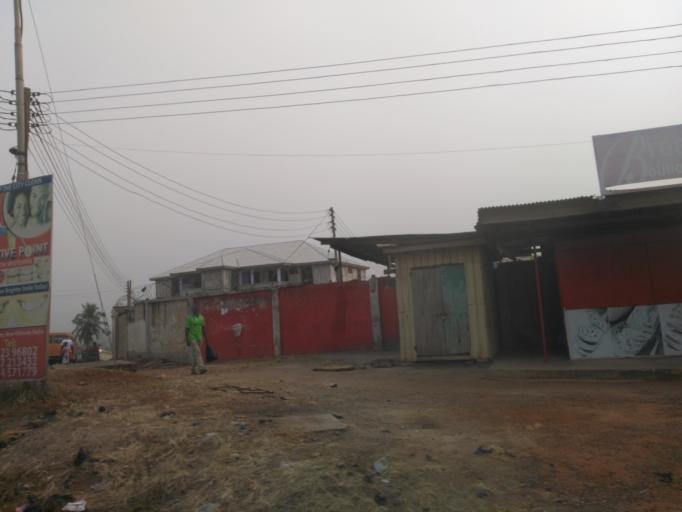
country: GH
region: Ashanti
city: Tafo
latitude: 6.7105
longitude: -1.6098
